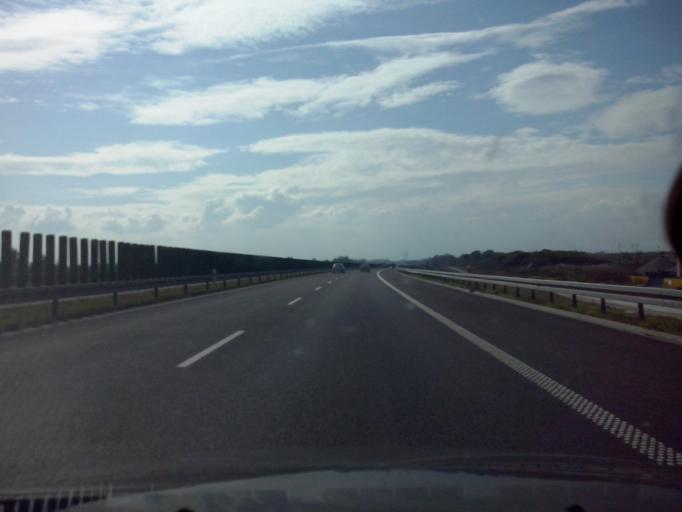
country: PL
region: Lesser Poland Voivodeship
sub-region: Powiat tarnowski
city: Lukowa
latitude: 50.0587
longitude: 20.9418
